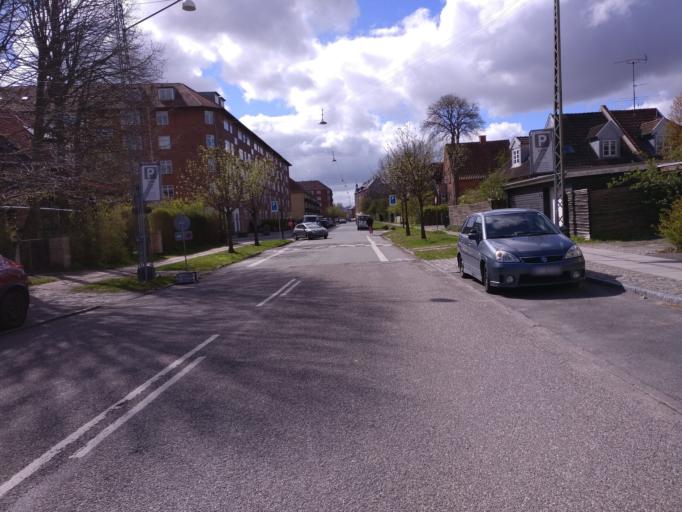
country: DK
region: Capital Region
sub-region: Kobenhavn
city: Vanlose
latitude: 55.6695
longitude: 12.5068
